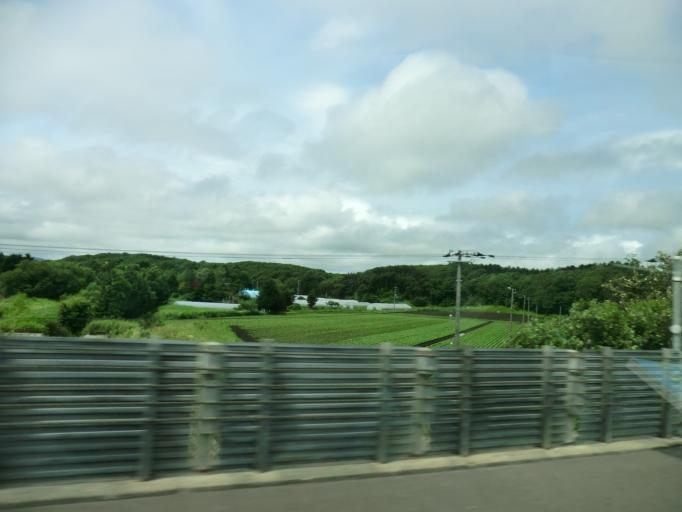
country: JP
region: Hokkaido
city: Kitahiroshima
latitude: 42.8906
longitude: 141.5491
